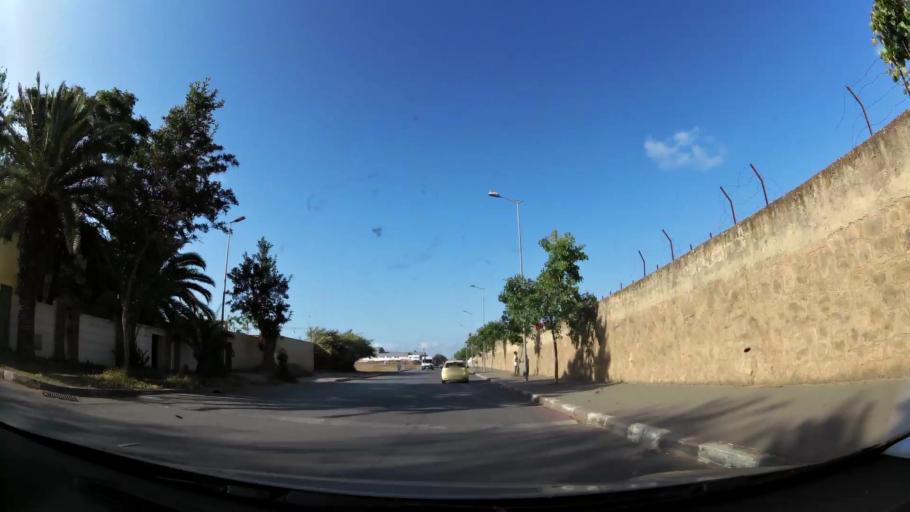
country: MA
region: Rabat-Sale-Zemmour-Zaer
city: Sale
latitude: 34.0531
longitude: -6.7978
